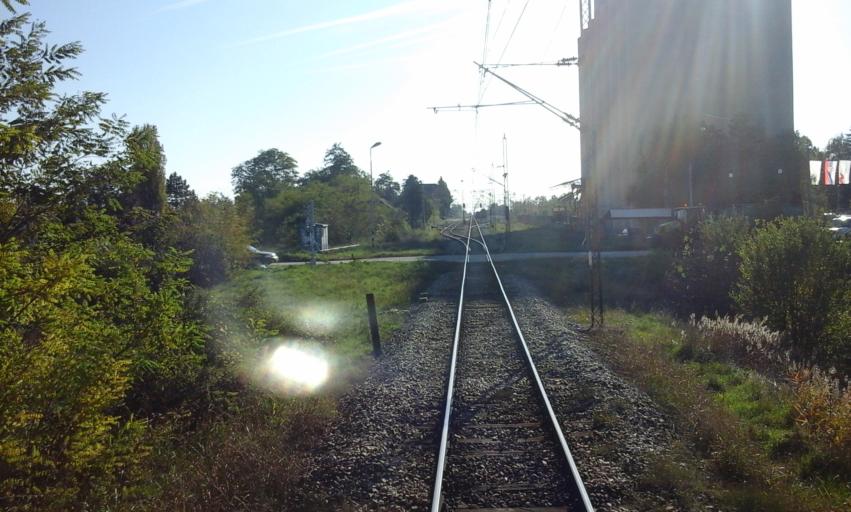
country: RS
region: Autonomna Pokrajina Vojvodina
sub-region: Severnobacki Okrug
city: Backa Topola
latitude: 45.9431
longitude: 19.6688
